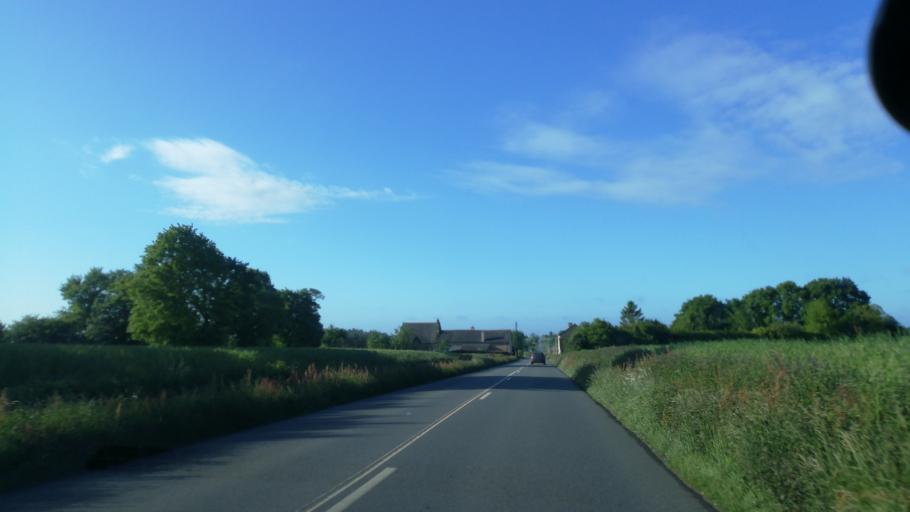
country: FR
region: Brittany
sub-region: Departement d'Ille-et-Vilaine
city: Irodouer
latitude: 48.2283
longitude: -1.9456
